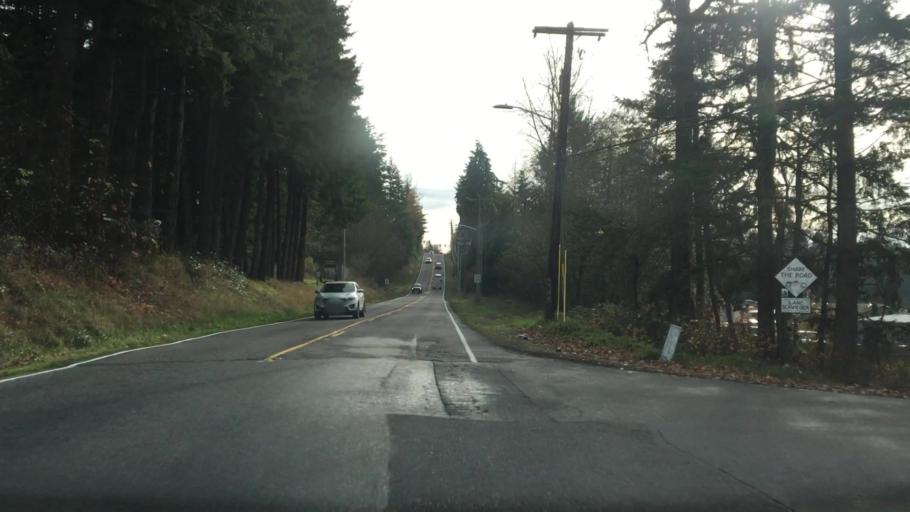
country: US
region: Washington
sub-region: Pierce County
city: Frederickson
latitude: 47.1150
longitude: -122.3255
